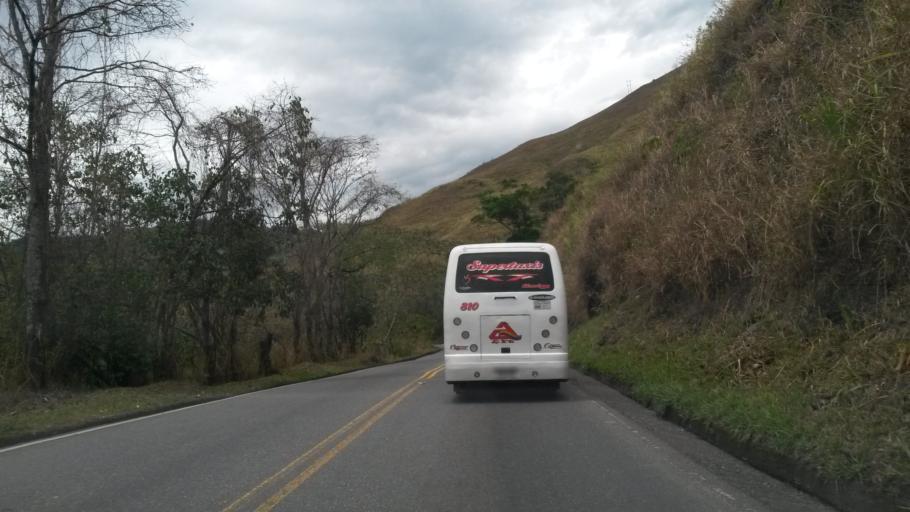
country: CO
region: Cauca
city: Rosas
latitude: 2.2764
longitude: -76.7088
